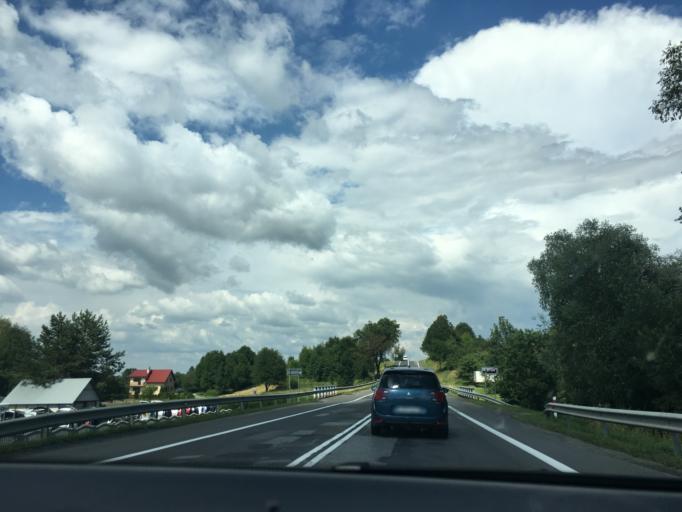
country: PL
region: Subcarpathian Voivodeship
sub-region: Powiat krosnienski
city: Dukla
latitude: 49.5962
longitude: 21.7177
